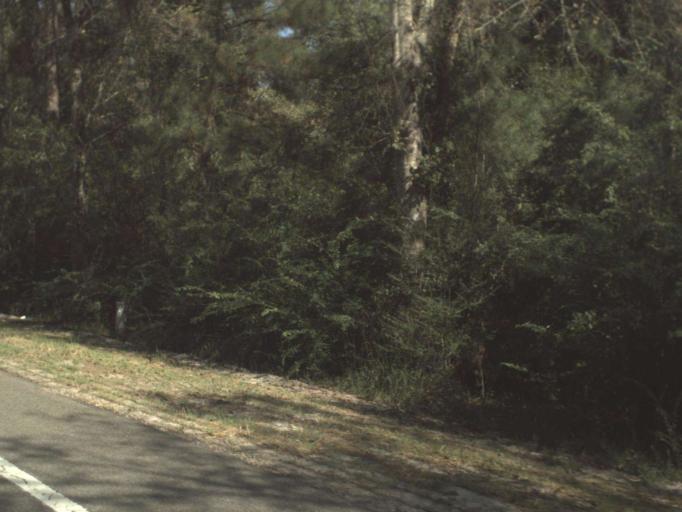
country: US
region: Florida
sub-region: Walton County
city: DeFuniak Springs
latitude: 30.8740
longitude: -86.1221
